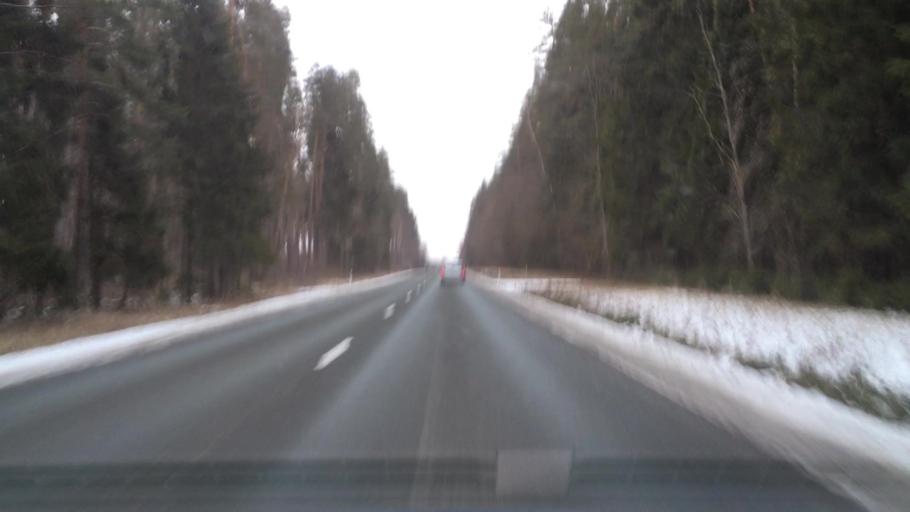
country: LV
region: Valmieras Rajons
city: Valmiera
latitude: 57.5037
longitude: 25.4200
